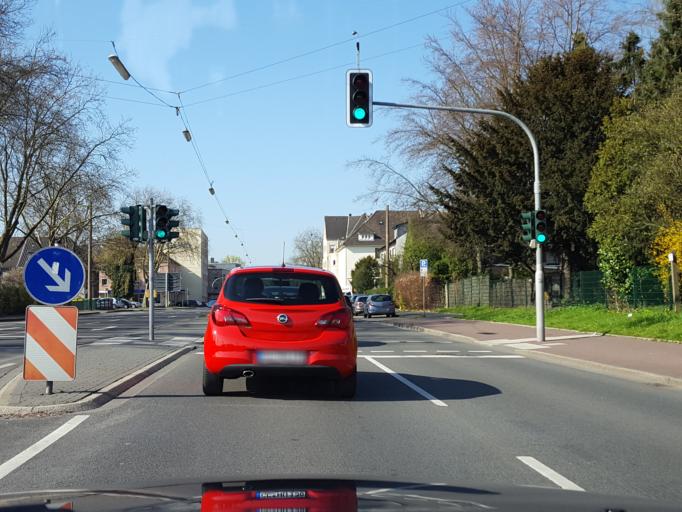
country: DE
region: North Rhine-Westphalia
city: Castrop-Rauxel
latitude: 51.5825
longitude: 7.3107
